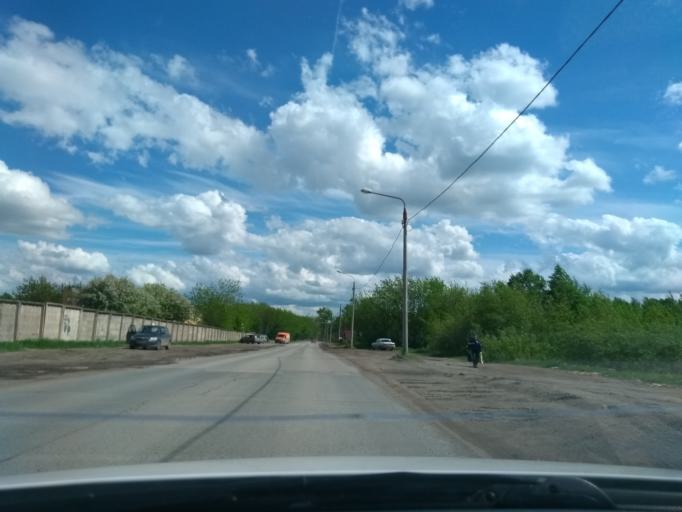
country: RU
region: Perm
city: Kondratovo
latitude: 58.0077
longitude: 56.1138
